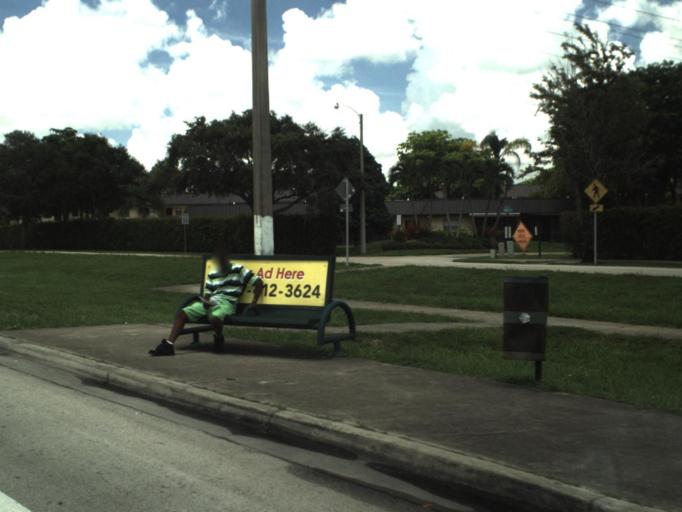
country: US
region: Florida
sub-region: Broward County
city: Miramar
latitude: 26.0087
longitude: -80.2675
